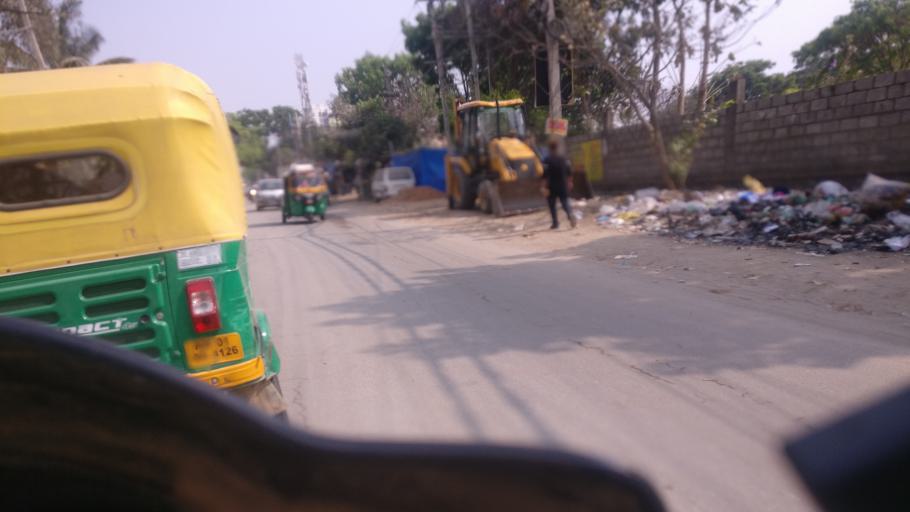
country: IN
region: Karnataka
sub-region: Bangalore Urban
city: Bangalore
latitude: 12.8879
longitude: 77.6728
